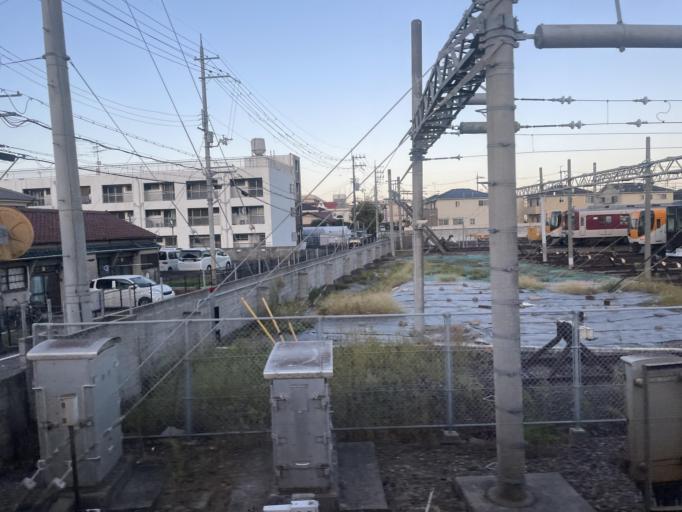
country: JP
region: Osaka
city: Yao
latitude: 34.6139
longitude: 135.6255
